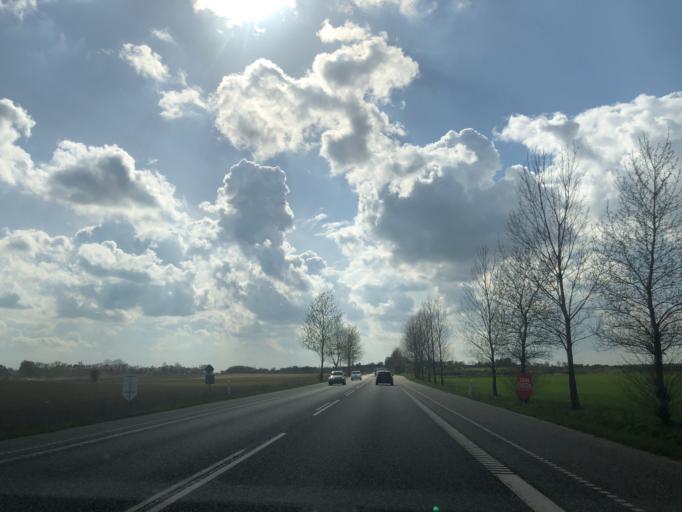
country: DK
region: Capital Region
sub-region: Hillerod Kommune
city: Hillerod
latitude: 55.9053
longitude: 12.2580
